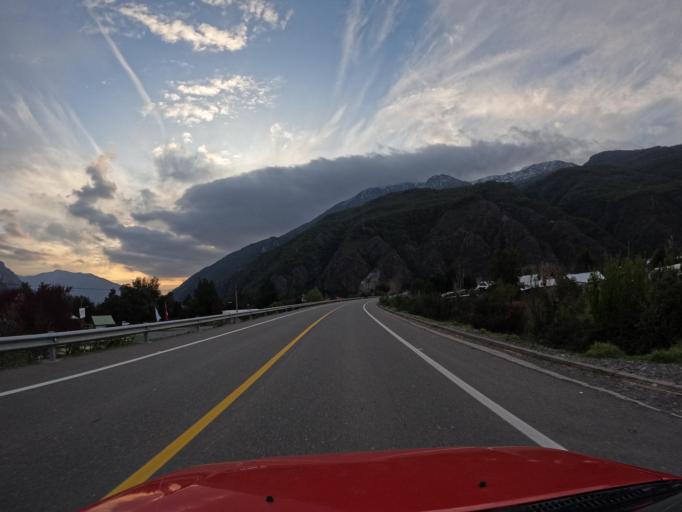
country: CL
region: Maule
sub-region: Provincia de Linares
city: Colbun
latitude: -35.7156
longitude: -71.1192
